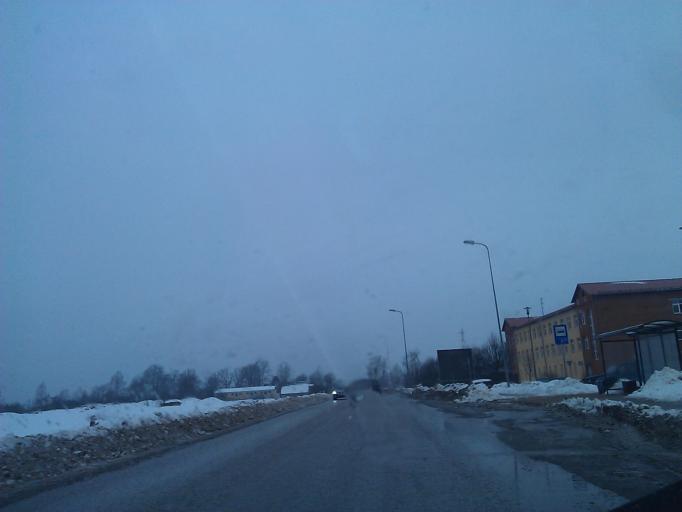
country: LV
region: Cesu Rajons
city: Cesis
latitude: 57.2981
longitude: 25.3003
